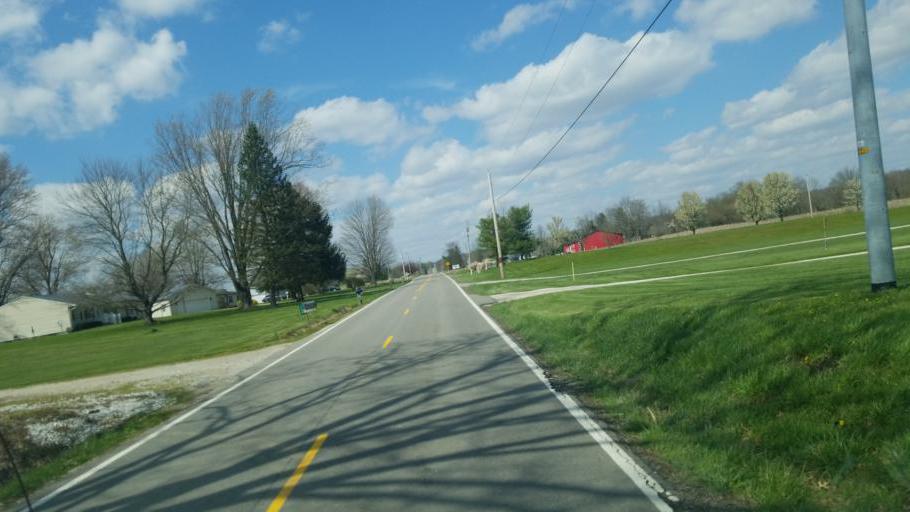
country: US
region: Ohio
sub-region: Licking County
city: Johnstown
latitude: 40.1096
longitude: -82.6163
